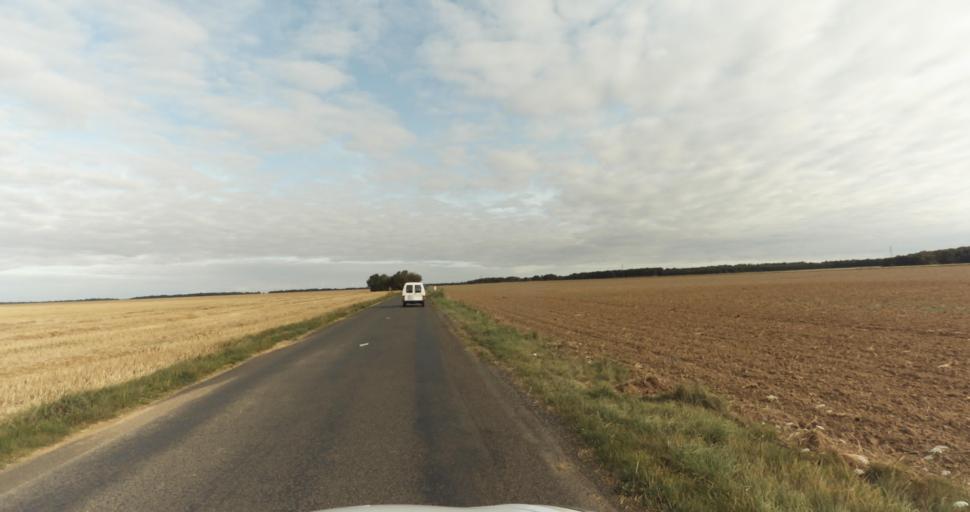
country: FR
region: Centre
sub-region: Departement d'Eure-et-Loir
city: Vert-en-Drouais
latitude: 48.7770
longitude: 1.2984
